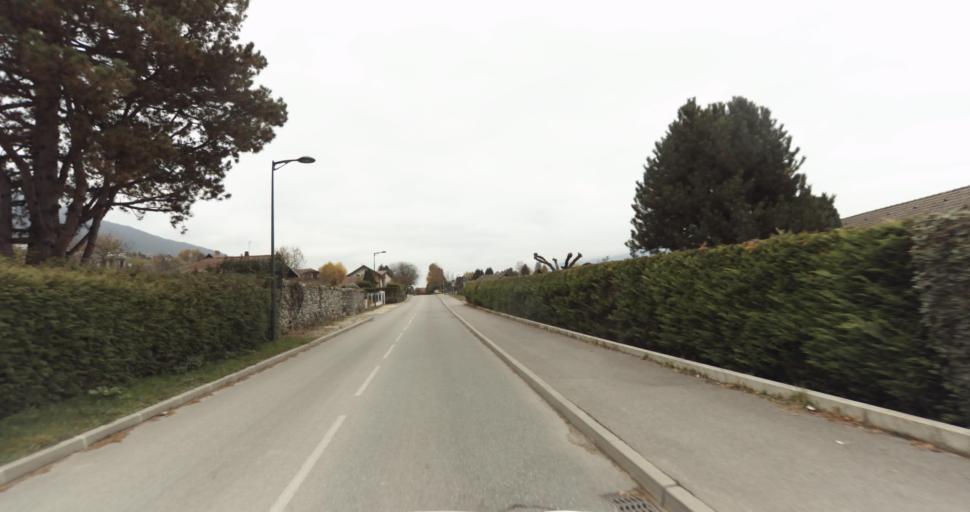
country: FR
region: Rhone-Alpes
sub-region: Departement de la Haute-Savoie
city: Saint-Jorioz
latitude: 45.8278
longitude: 6.1520
